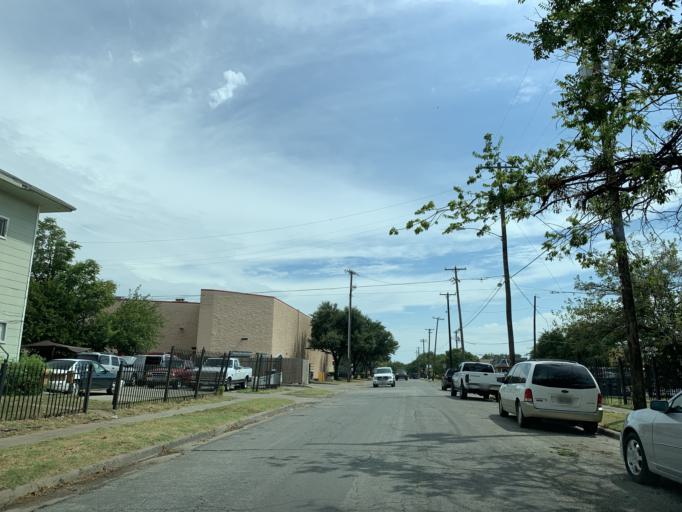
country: US
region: Texas
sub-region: Dallas County
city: Dallas
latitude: 32.7450
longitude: -96.8339
